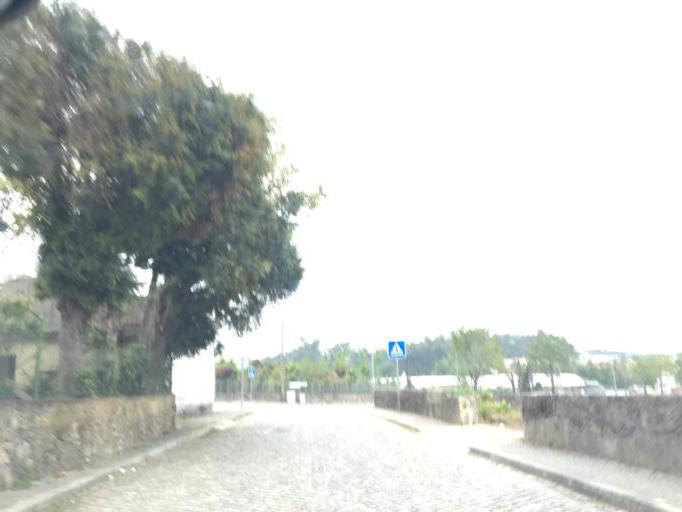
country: PT
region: Porto
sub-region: Maia
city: Nogueira
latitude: 41.2443
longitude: -8.6017
